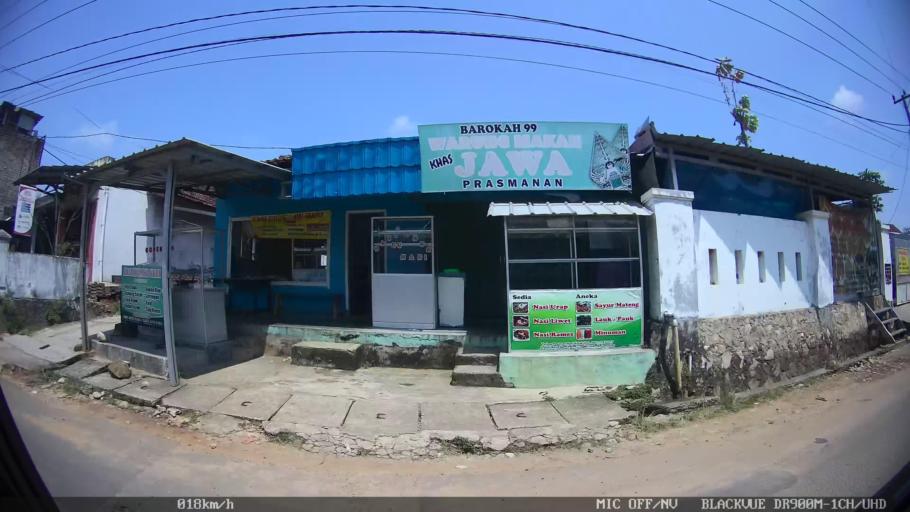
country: ID
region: Lampung
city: Kedaton
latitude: -5.3640
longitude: 105.2680
